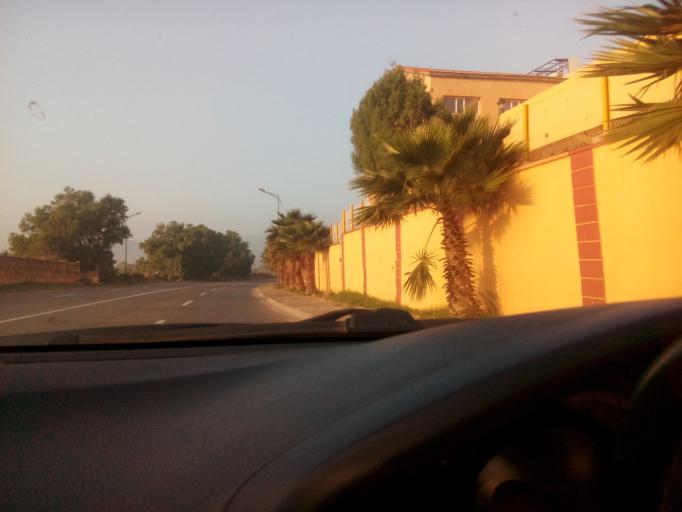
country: DZ
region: Oran
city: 'Ain el Turk
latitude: 35.7101
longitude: -0.8732
